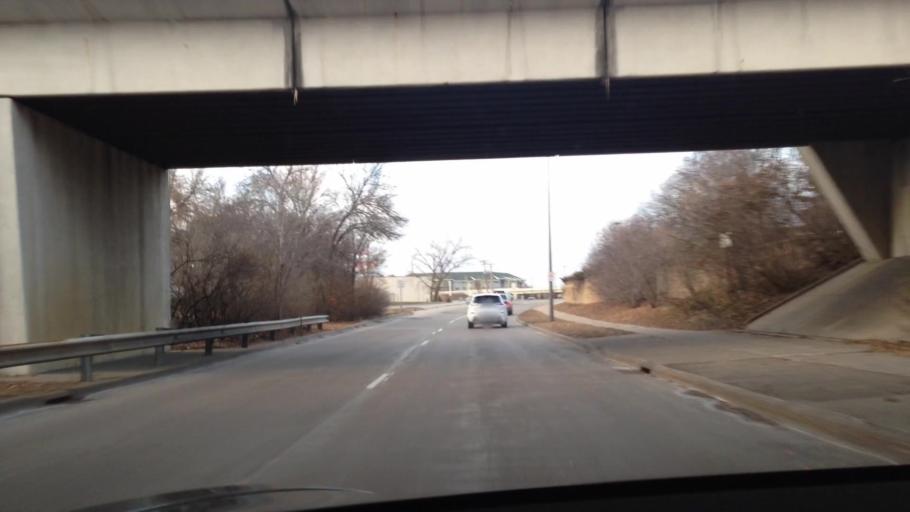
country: US
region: Minnesota
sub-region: Hennepin County
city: Saint Louis Park
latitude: 44.9342
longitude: -93.3676
